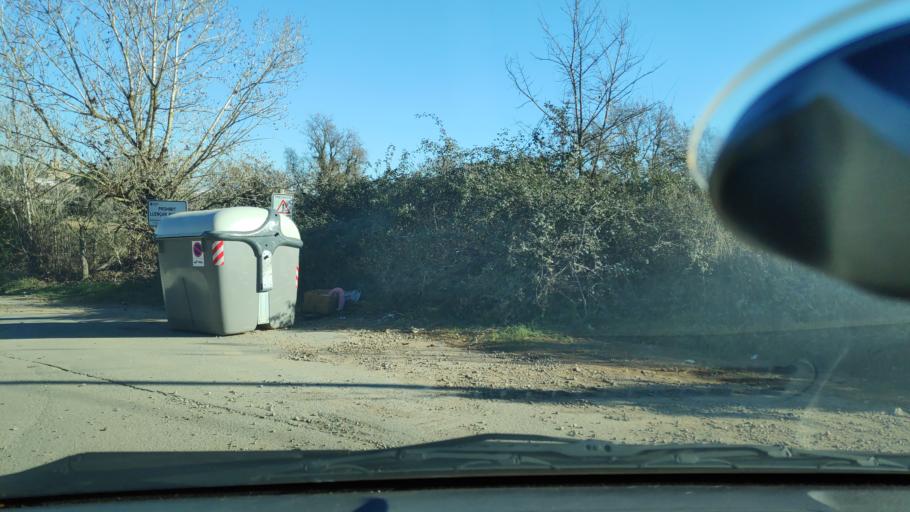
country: ES
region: Catalonia
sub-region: Provincia de Barcelona
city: Sant Quirze del Valles
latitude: 41.5195
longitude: 2.0952
